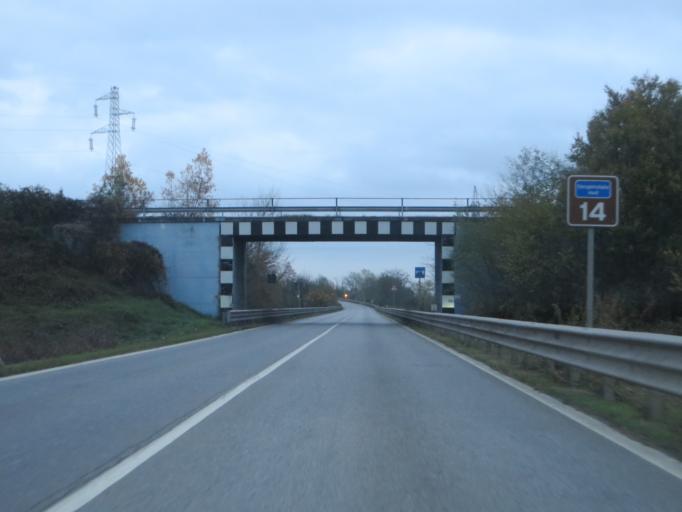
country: IT
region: Lombardy
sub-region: Provincia di Brescia
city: Molinetto
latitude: 45.4790
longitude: 10.3528
